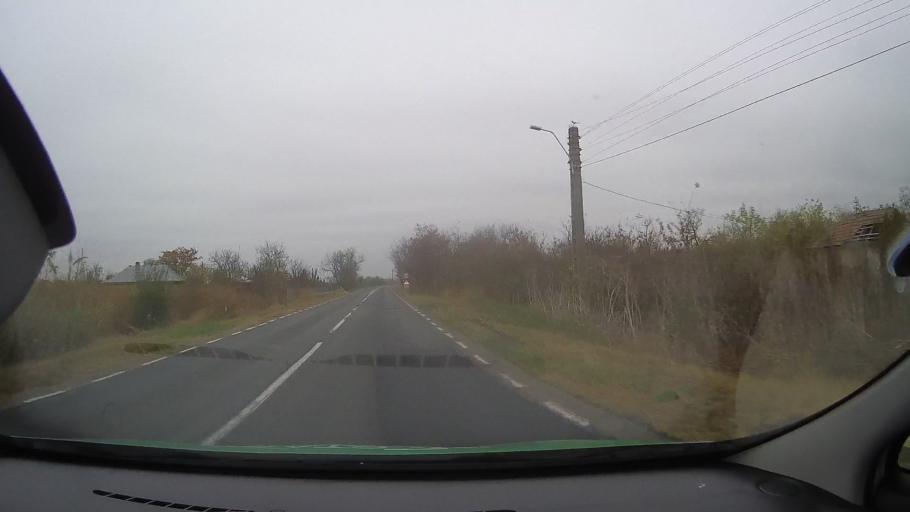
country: RO
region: Braila
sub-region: Comuna Baraganul
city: Baraganul
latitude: 44.7984
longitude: 27.5128
